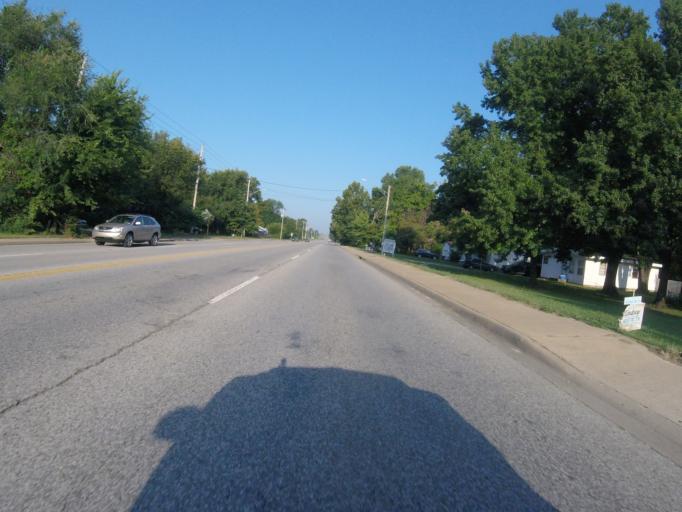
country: US
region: Arkansas
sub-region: Washington County
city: Fayetteville
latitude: 36.0781
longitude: -94.1906
